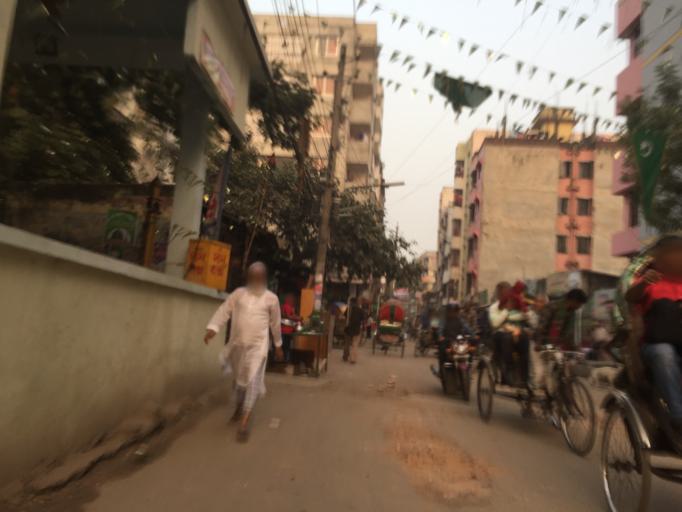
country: BD
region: Dhaka
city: Azimpur
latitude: 23.7704
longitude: 90.3625
